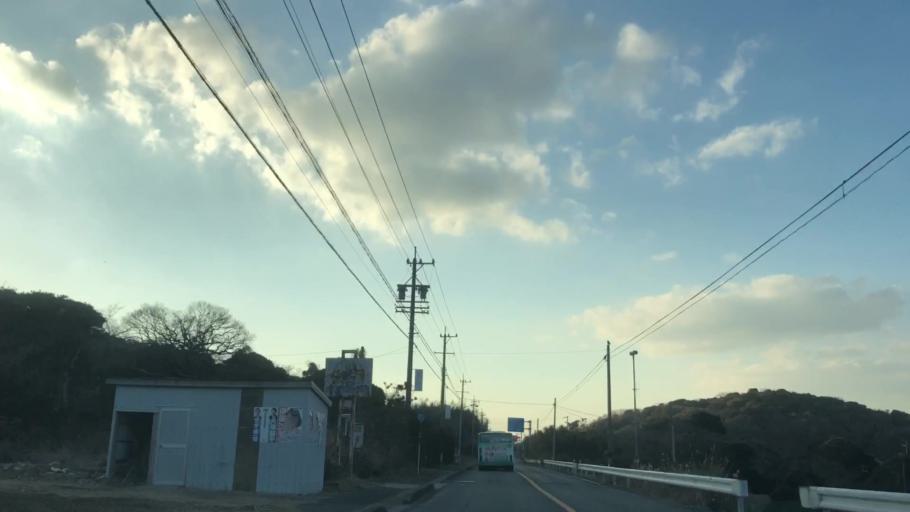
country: JP
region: Aichi
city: Tahara
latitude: 34.6659
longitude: 137.1921
